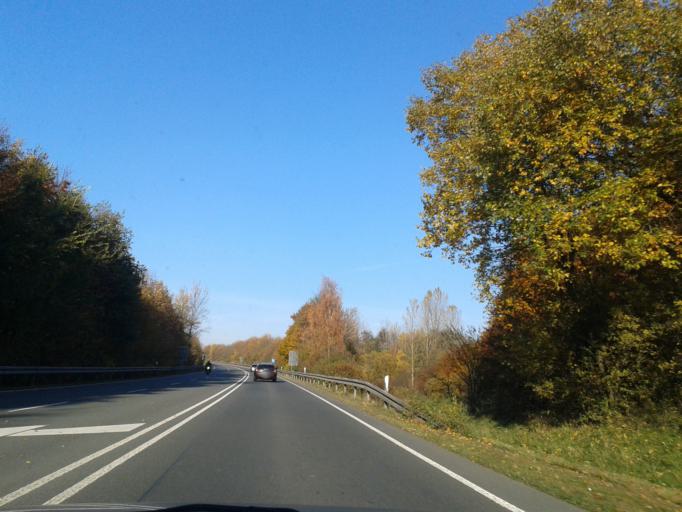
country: DE
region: North Rhine-Westphalia
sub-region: Regierungsbezirk Arnsberg
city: Ruthen
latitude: 51.4995
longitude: 8.4517
